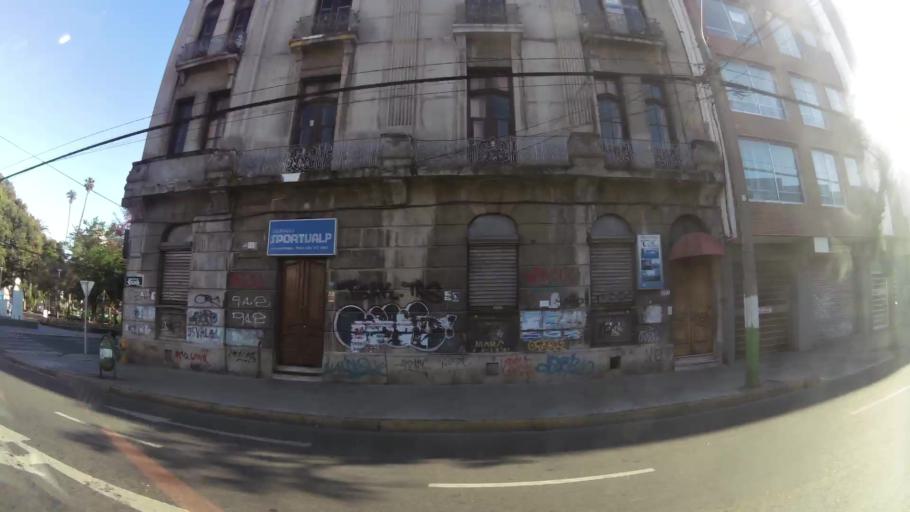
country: CL
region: Valparaiso
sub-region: Provincia de Valparaiso
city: Valparaiso
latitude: -33.0487
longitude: -71.6134
